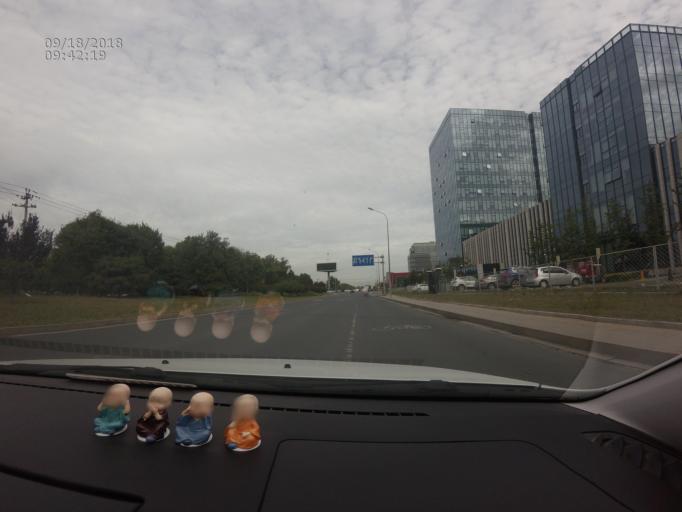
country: CN
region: Beijing
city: Xibeiwang
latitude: 40.0708
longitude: 116.2391
